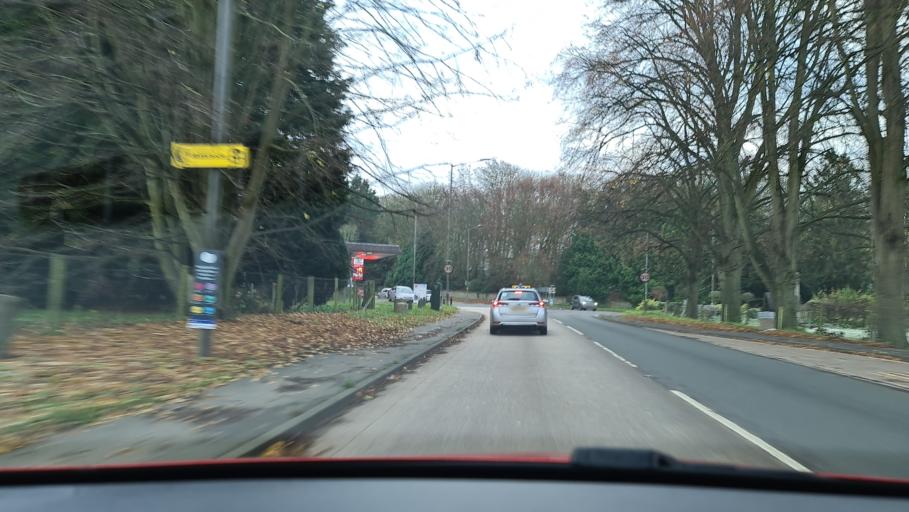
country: GB
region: England
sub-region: Buckinghamshire
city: High Wycombe
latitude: 51.6453
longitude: -0.7964
